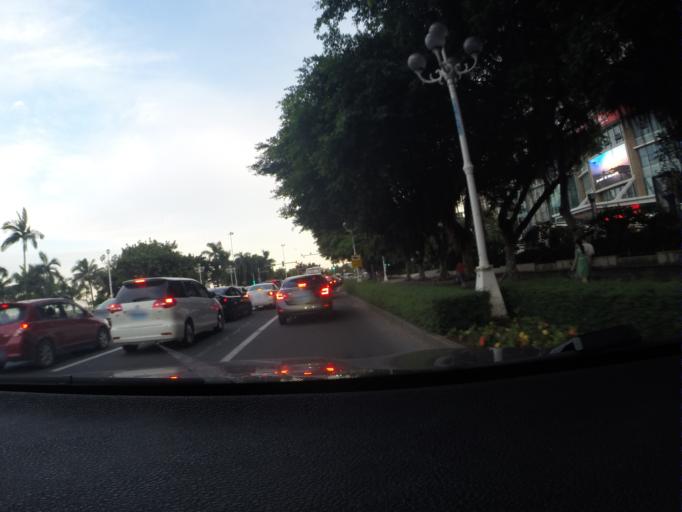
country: CN
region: Guangdong
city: Zhuhai
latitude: 22.2790
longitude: 113.5764
